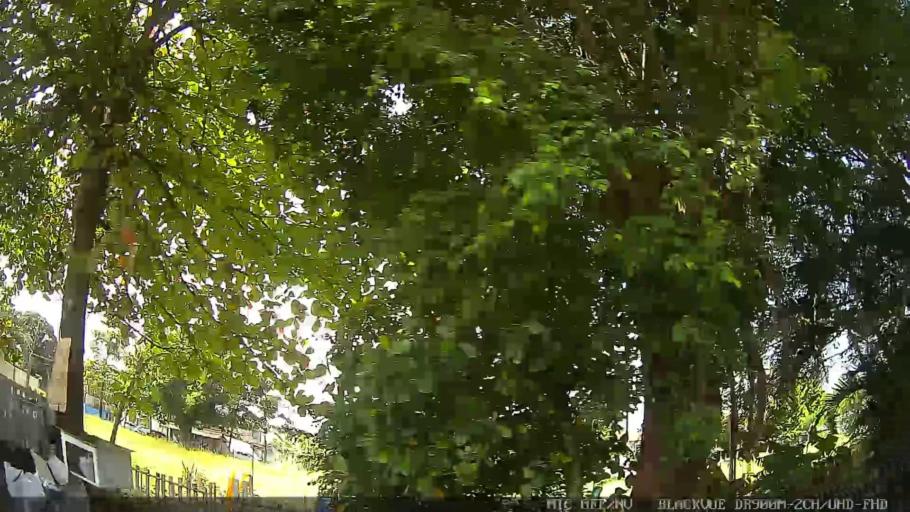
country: BR
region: Sao Paulo
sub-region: Santos
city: Santos
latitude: -23.9412
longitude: -46.2983
